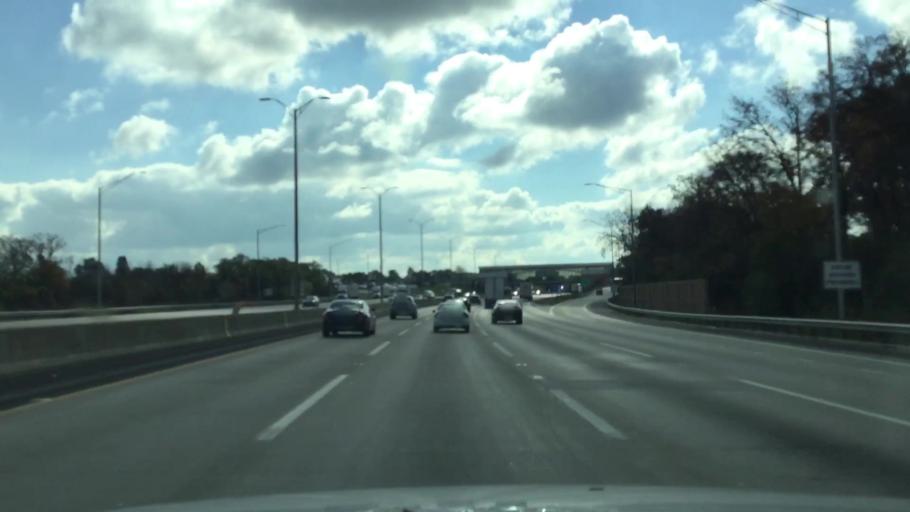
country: US
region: Illinois
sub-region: Lake County
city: Green Oaks
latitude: 42.2578
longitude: -87.9020
